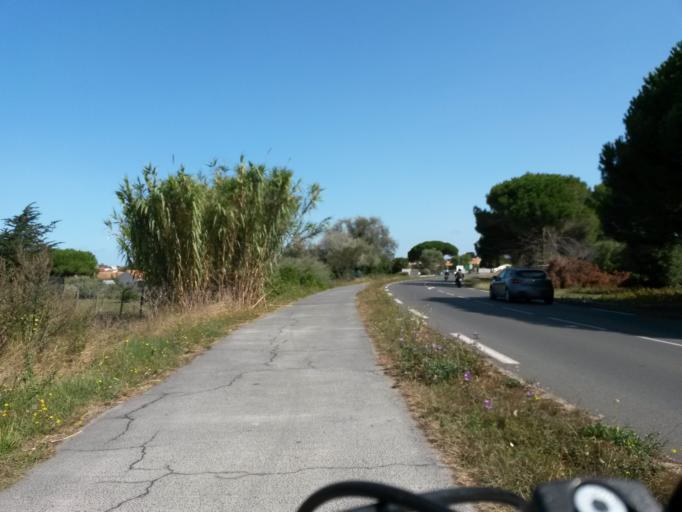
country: FR
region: Poitou-Charentes
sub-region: Departement de la Charente-Maritime
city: Saint-Martin-de-Re
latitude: 46.1866
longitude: -1.3712
